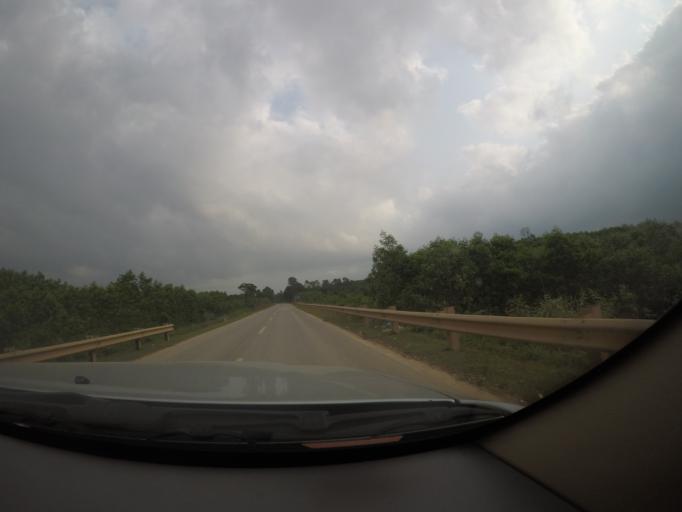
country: VN
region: Quang Tri
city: Ho Xa
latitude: 17.0574
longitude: 106.8633
